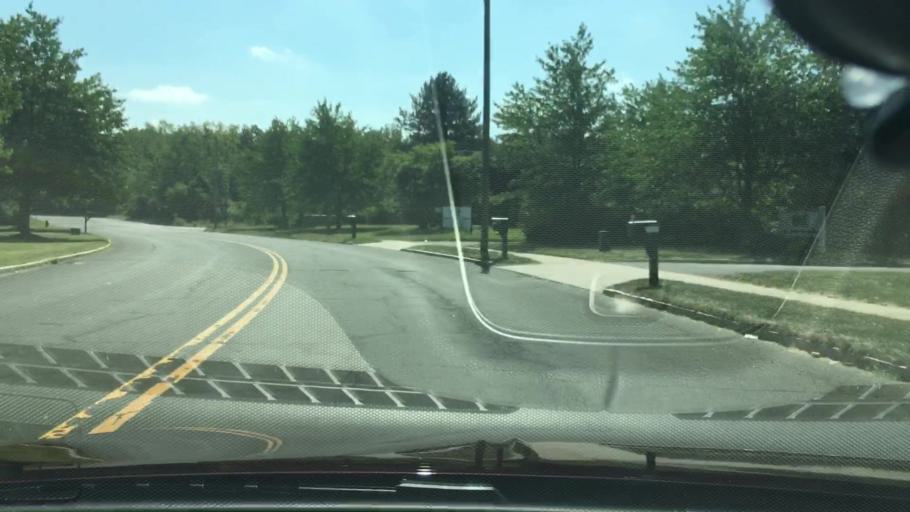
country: US
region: Connecticut
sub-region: Hartford County
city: Bristol
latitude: 41.6499
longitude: -72.9102
